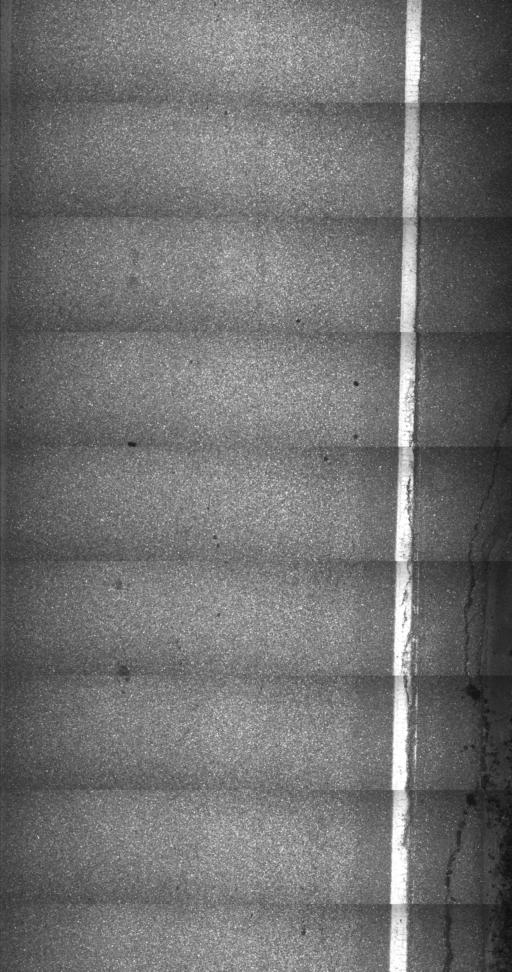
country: US
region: Vermont
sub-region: Orange County
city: Randolph
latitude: 43.9651
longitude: -72.8423
